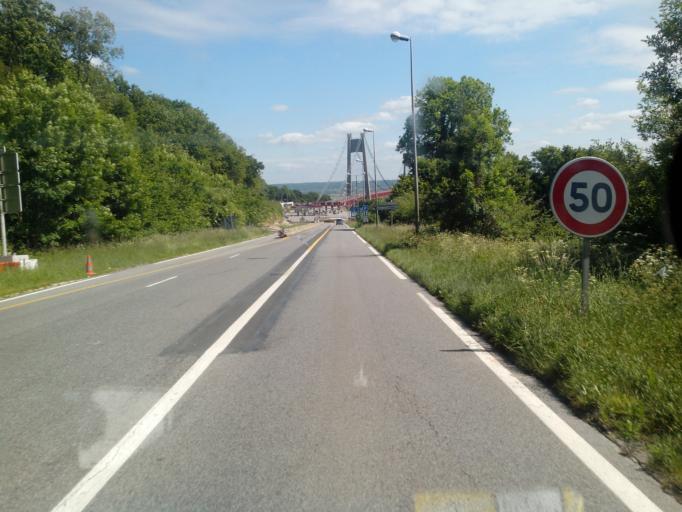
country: FR
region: Haute-Normandie
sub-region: Departement de la Seine-Maritime
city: Tancarville
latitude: 49.4799
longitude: 0.4550
